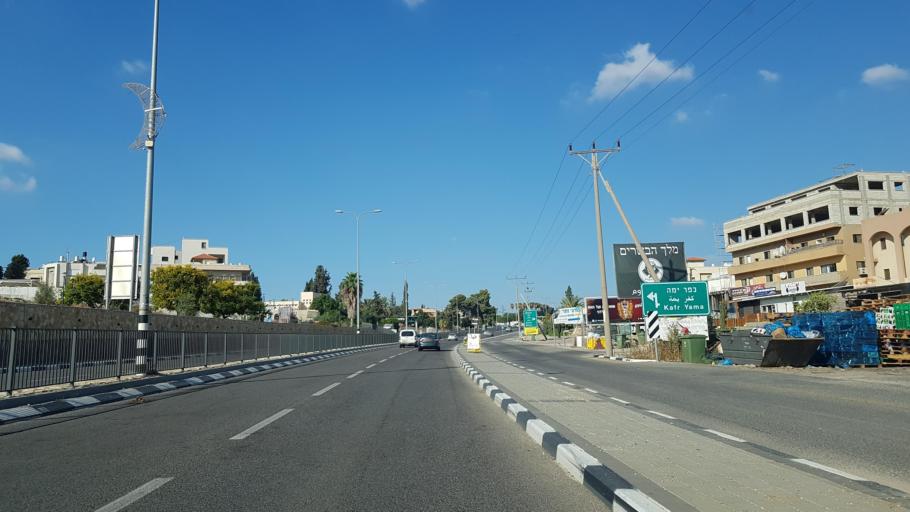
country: PS
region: West Bank
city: Zayta
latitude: 32.3645
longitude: 35.0310
